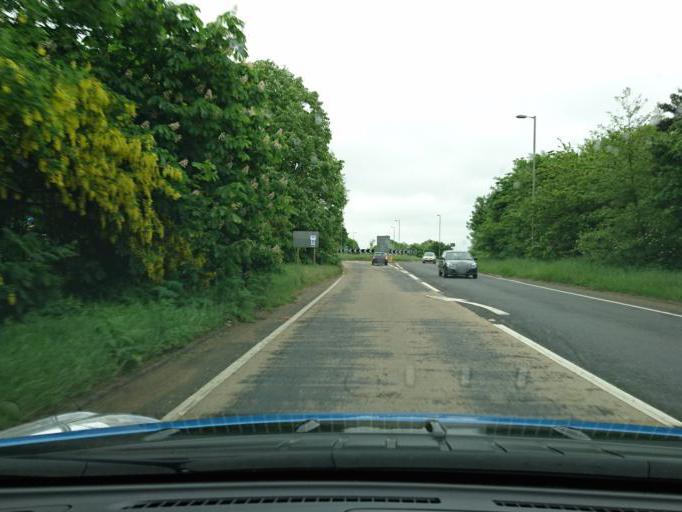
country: GB
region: England
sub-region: Oxfordshire
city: Faringdon
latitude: 51.6541
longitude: -1.5688
